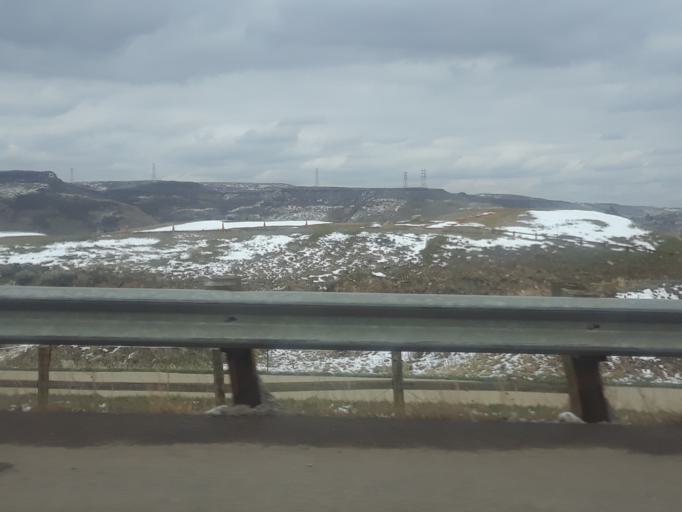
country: US
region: Colorado
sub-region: Jefferson County
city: Golden
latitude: 39.7393
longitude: -105.2182
